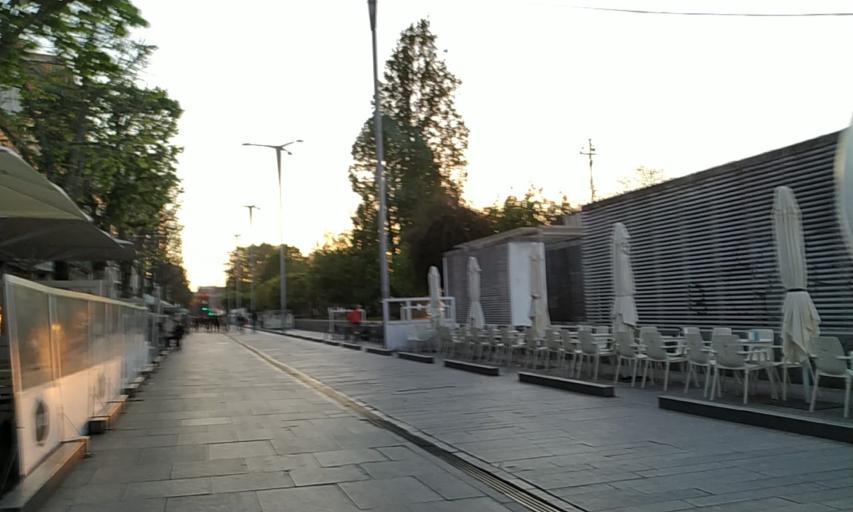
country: ES
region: Galicia
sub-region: Provincia de Pontevedra
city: Vigo
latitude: 42.2406
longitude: -8.7207
